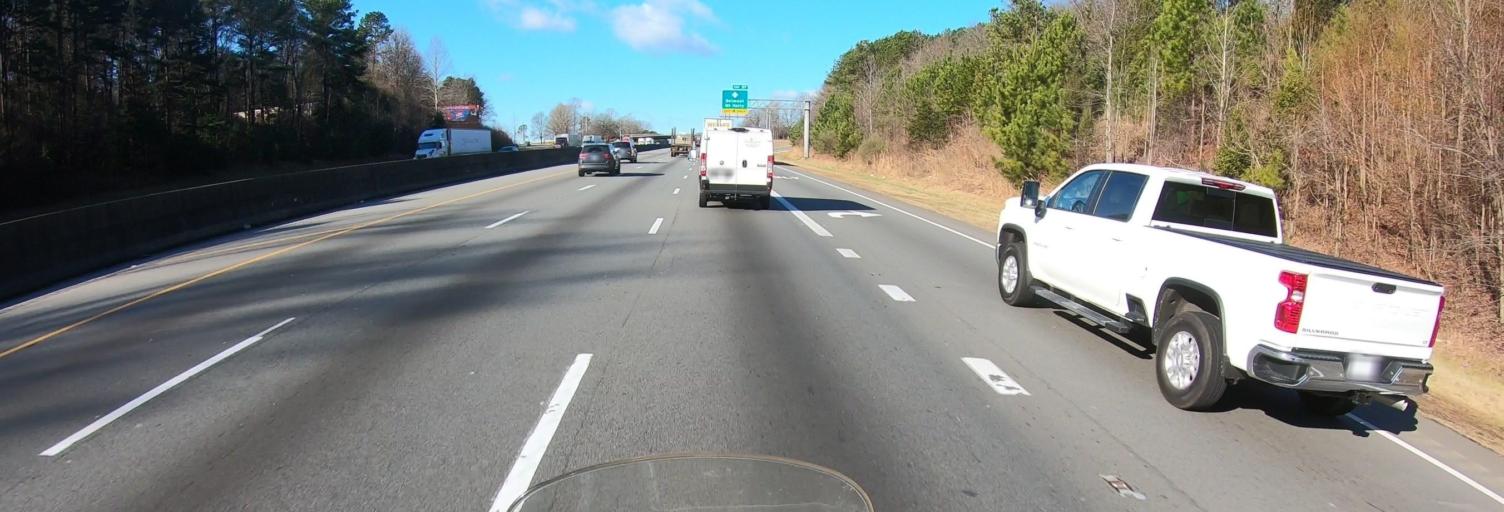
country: US
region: North Carolina
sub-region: Gaston County
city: Belmont
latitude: 35.2565
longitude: -81.0209
